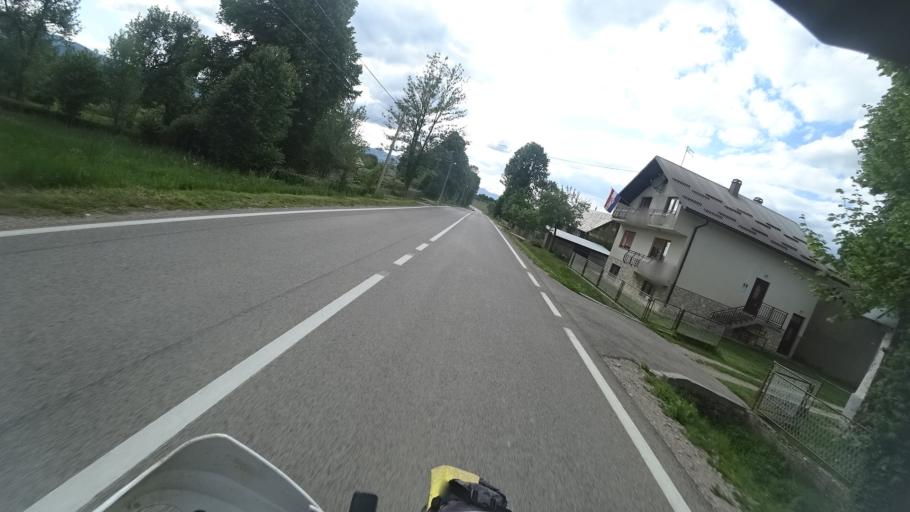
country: HR
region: Licko-Senjska
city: Gospic
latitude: 44.5094
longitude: 15.4355
